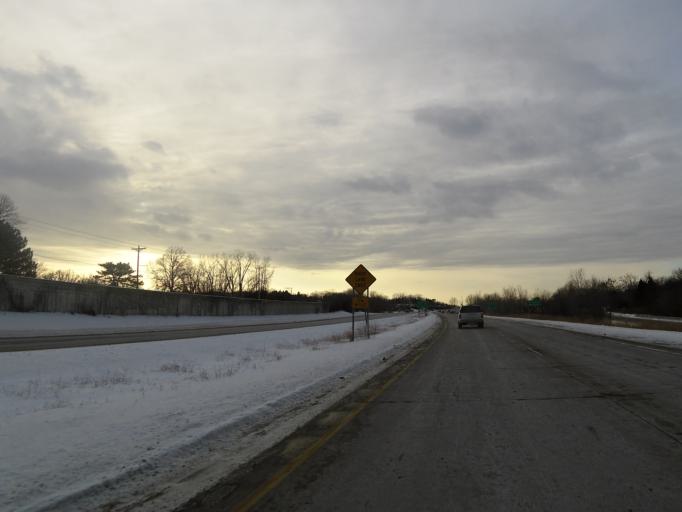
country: US
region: Minnesota
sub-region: Dakota County
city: Mendota Heights
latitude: 44.8837
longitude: -93.1565
